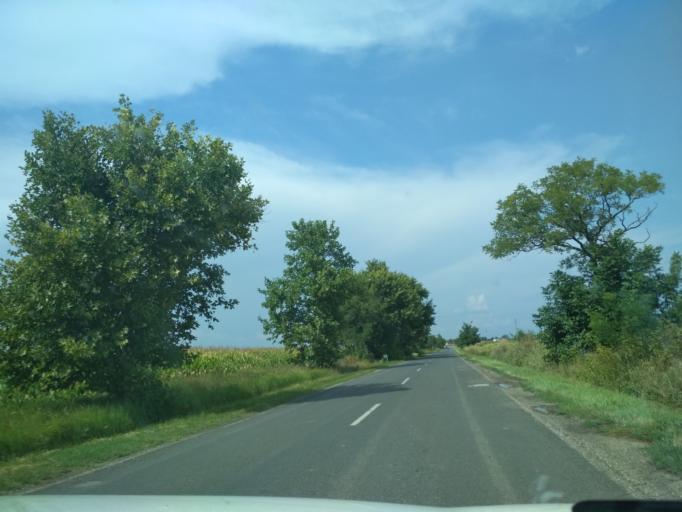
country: HU
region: Jasz-Nagykun-Szolnok
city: Tiszaszolos
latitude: 47.5423
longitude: 20.7189
